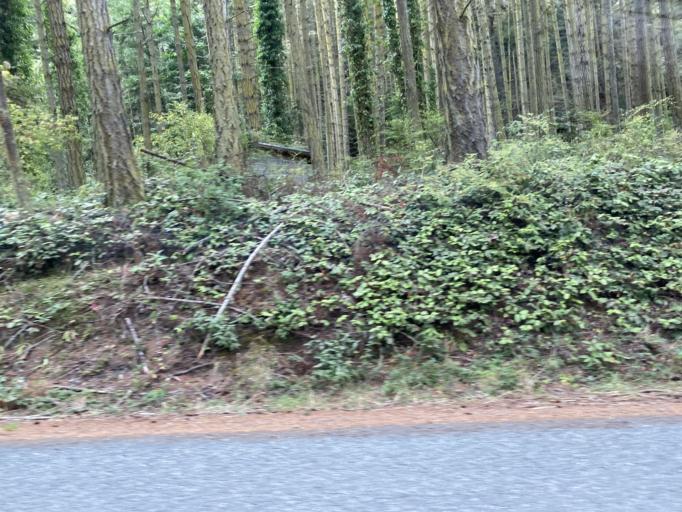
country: US
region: Washington
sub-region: Island County
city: Ault Field
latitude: 48.4204
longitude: -122.6611
